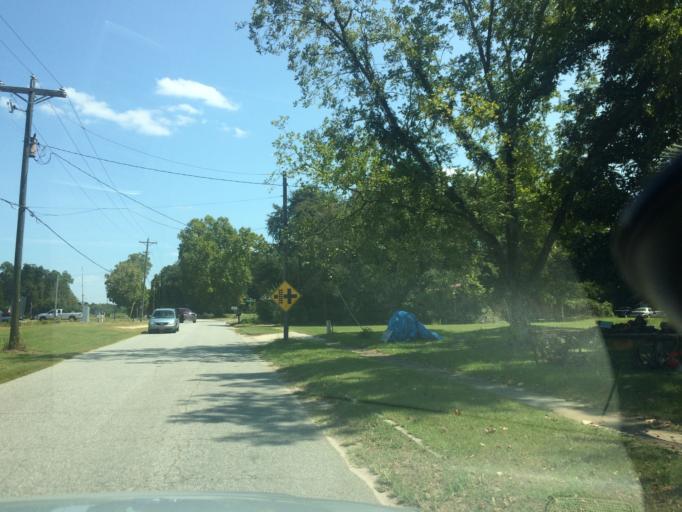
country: US
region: South Carolina
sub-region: Aiken County
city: Aiken
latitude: 33.5276
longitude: -81.6355
